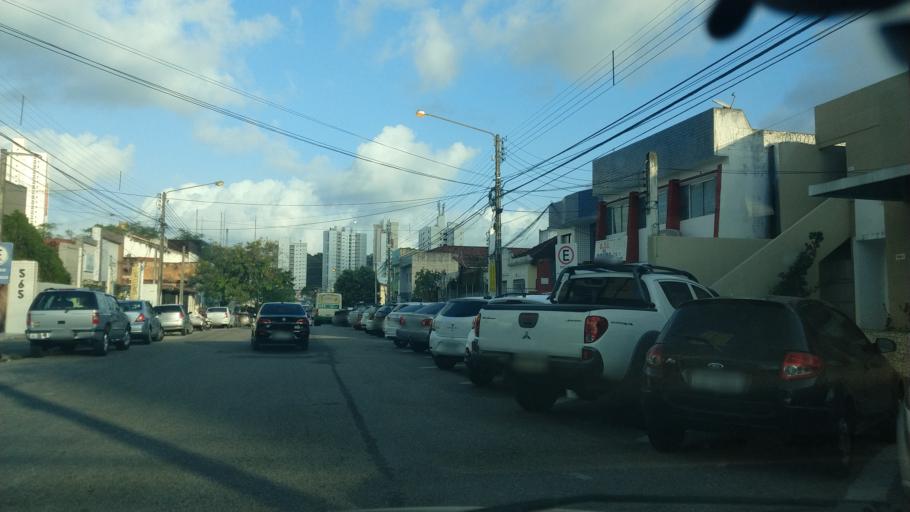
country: BR
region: Rio Grande do Norte
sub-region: Natal
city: Natal
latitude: -5.7879
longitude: -35.1996
